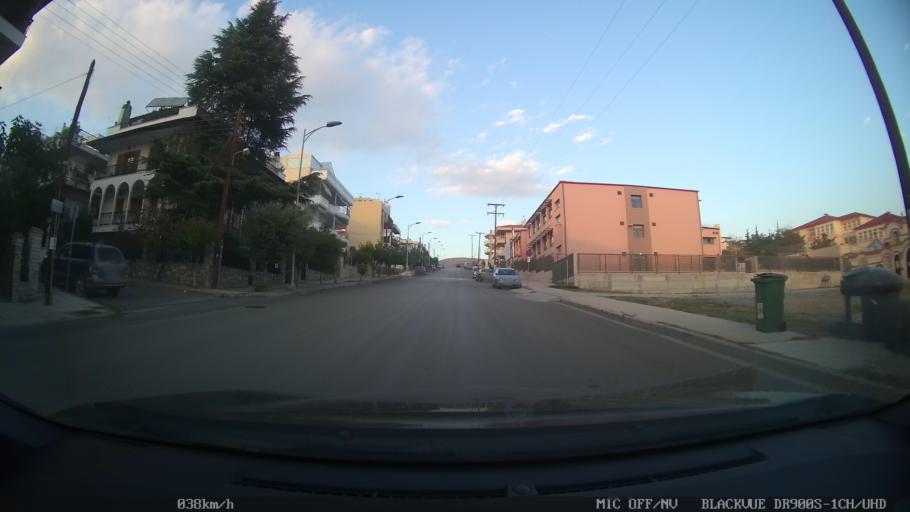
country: GR
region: Central Macedonia
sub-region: Nomos Thessalonikis
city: Pylaia
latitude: 40.6116
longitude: 22.9934
